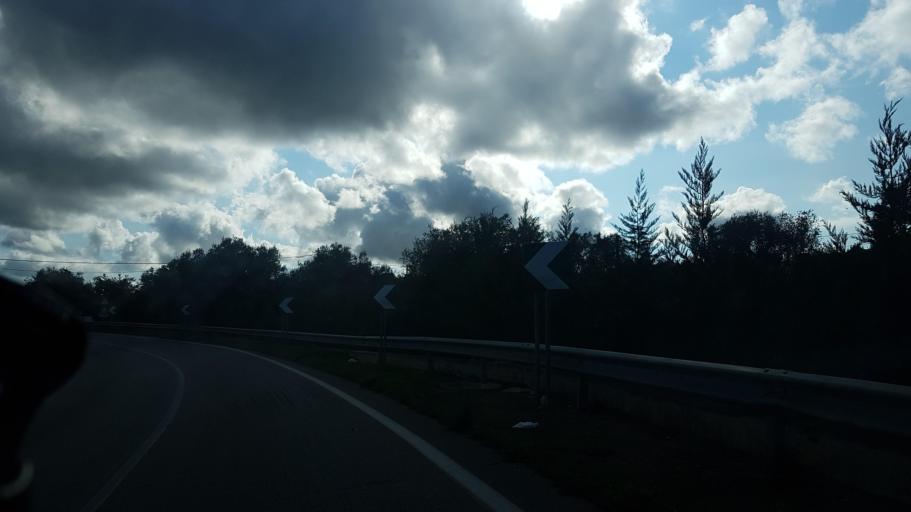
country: IT
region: Apulia
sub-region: Provincia di Brindisi
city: Ostuni
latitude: 40.6814
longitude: 17.5895
